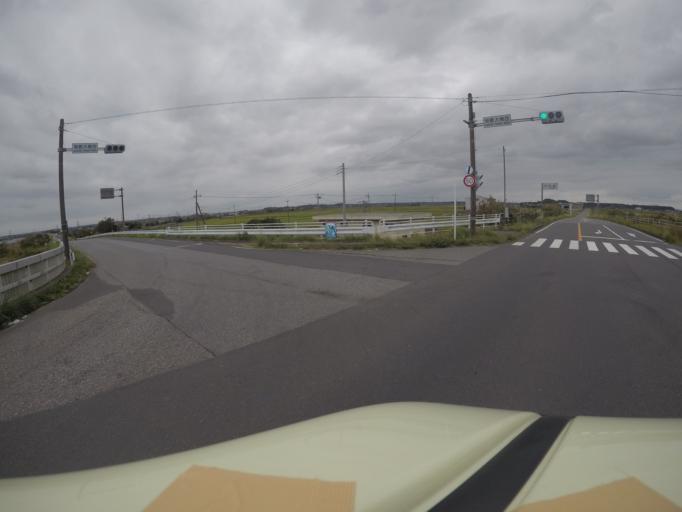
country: JP
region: Chiba
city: Katori-shi
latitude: 35.9589
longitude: 140.4573
